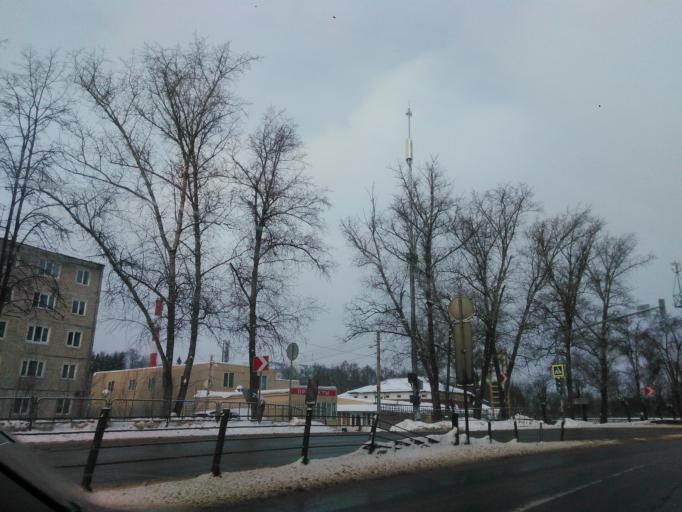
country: RU
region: Moskovskaya
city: Dedenevo
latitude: 56.2392
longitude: 37.5234
